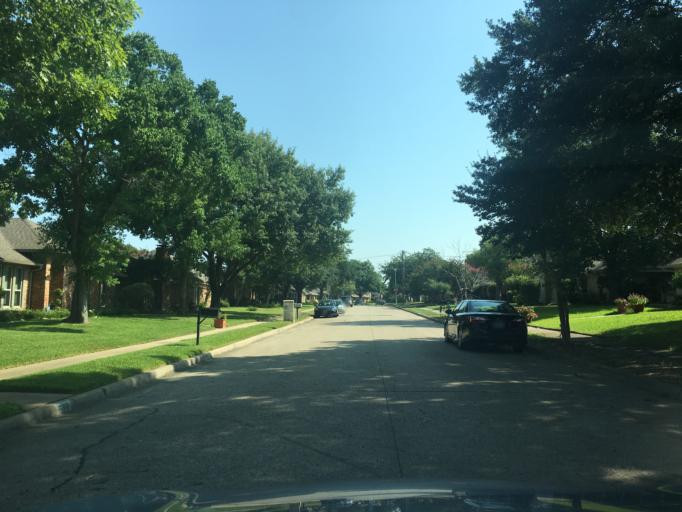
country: US
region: Texas
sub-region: Dallas County
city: Garland
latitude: 32.9432
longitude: -96.6366
